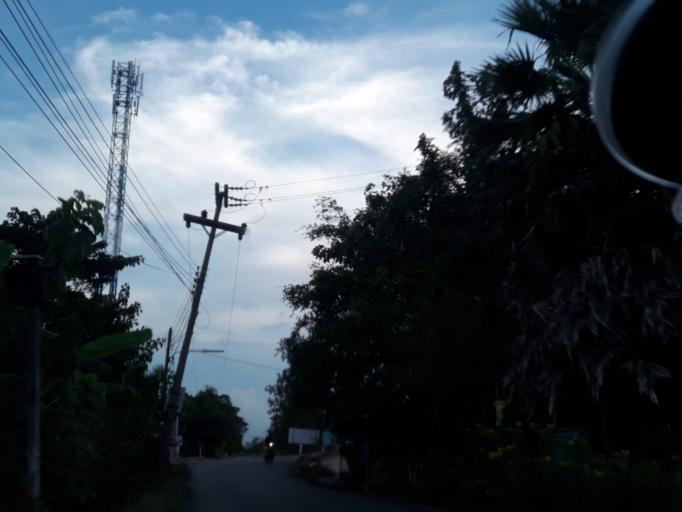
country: TH
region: Pathum Thani
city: Nong Suea
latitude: 14.1973
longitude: 100.8690
